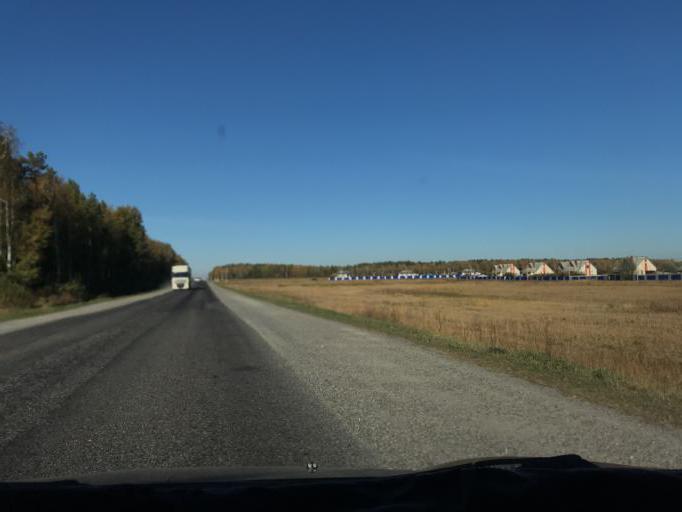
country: BY
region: Gomel
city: Yel'sk
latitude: 51.7936
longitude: 29.1992
